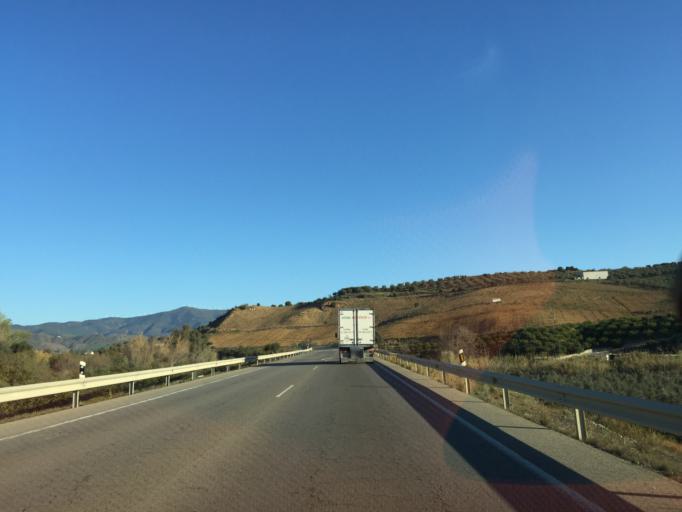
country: ES
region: Andalusia
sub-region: Provincia de Malaga
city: Pizarra
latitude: 36.7777
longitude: -4.7411
